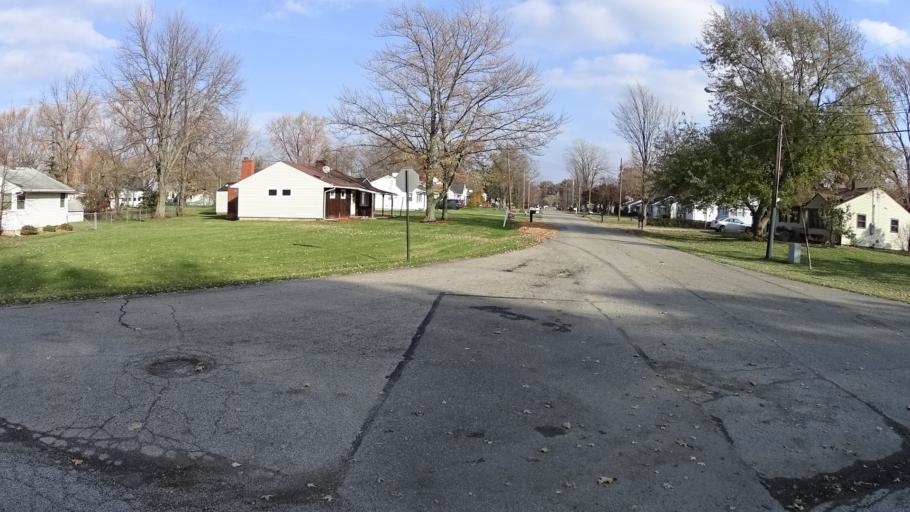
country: US
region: Ohio
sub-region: Lorain County
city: Elyria
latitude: 41.3903
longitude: -82.0877
